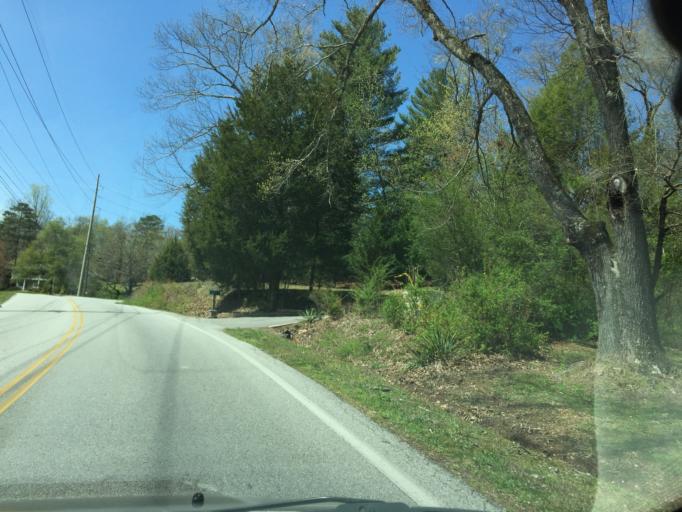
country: US
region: Tennessee
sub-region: Hamilton County
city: Middle Valley
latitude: 35.2037
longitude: -85.2095
